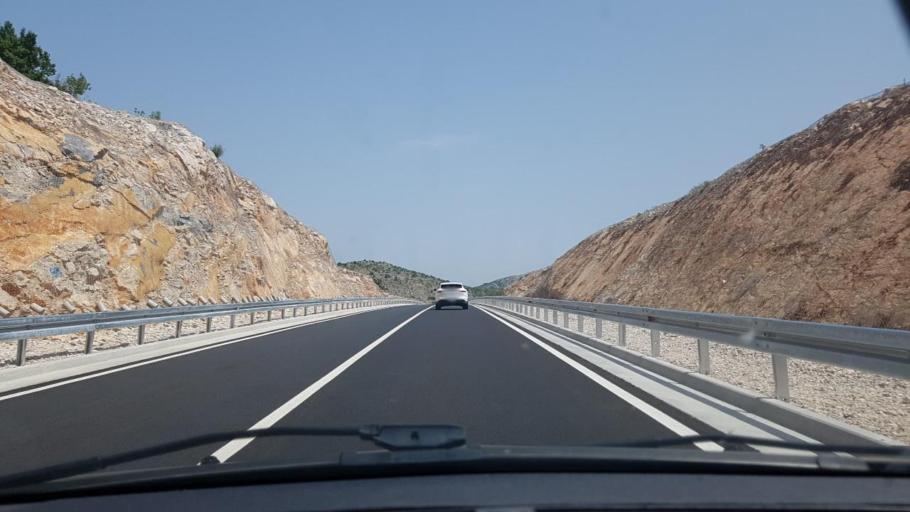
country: HR
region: Dubrovacko-Neretvanska
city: Podgora
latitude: 42.9468
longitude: 17.7660
